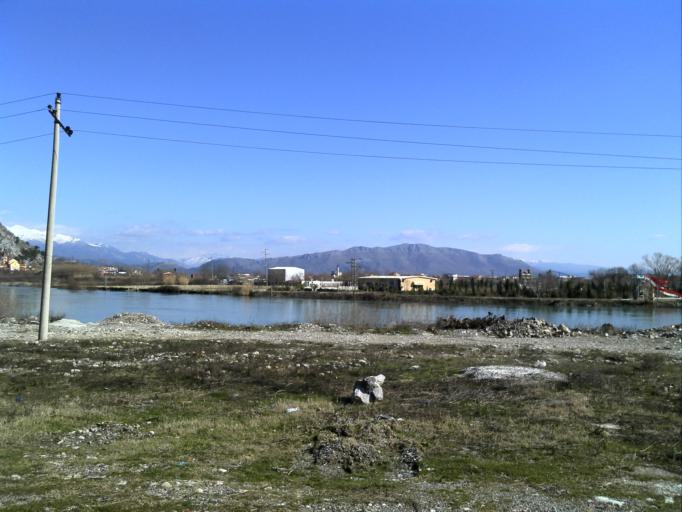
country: AL
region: Shkoder
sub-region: Rrethi i Shkodres
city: Berdica e Madhe
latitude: 42.0406
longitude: 19.4818
